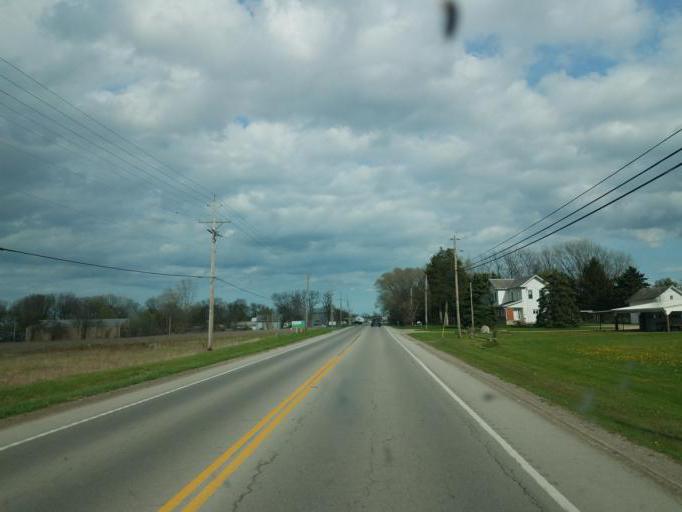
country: US
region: Ohio
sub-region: Ottawa County
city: Port Clinton
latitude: 41.5312
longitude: -82.8204
